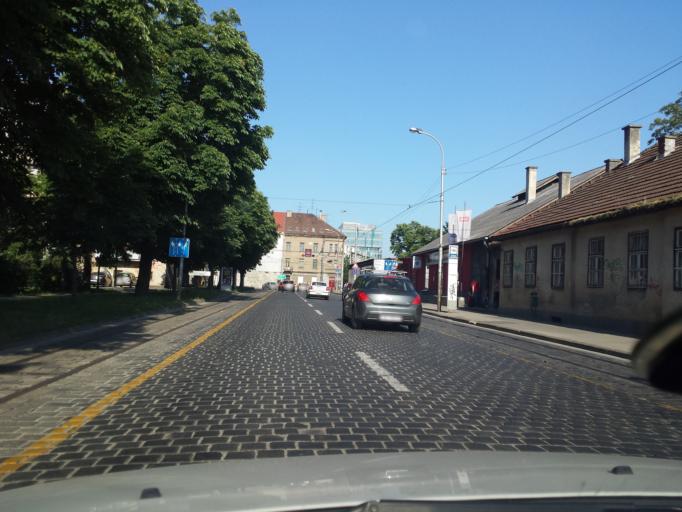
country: HR
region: Grad Zagreb
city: Zagreb - Centar
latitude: 45.8094
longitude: 15.9554
